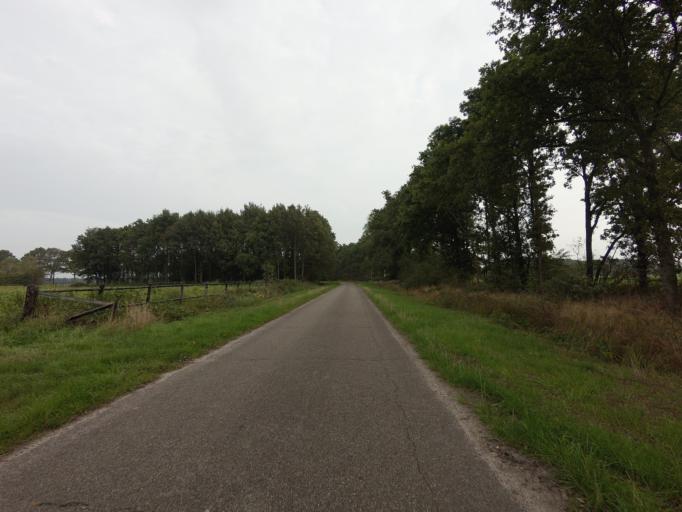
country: NL
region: Drenthe
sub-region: Gemeente Westerveld
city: Dwingeloo
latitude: 52.8603
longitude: 6.4117
